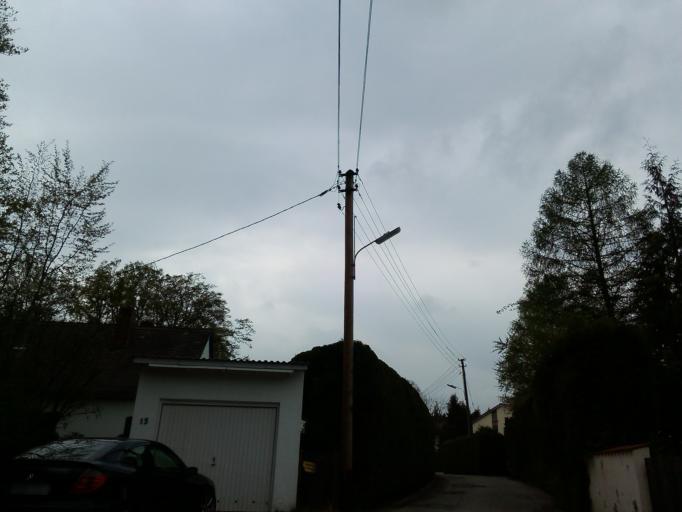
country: DE
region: Bavaria
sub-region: Upper Bavaria
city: Krailling
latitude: 48.0911
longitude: 11.3998
